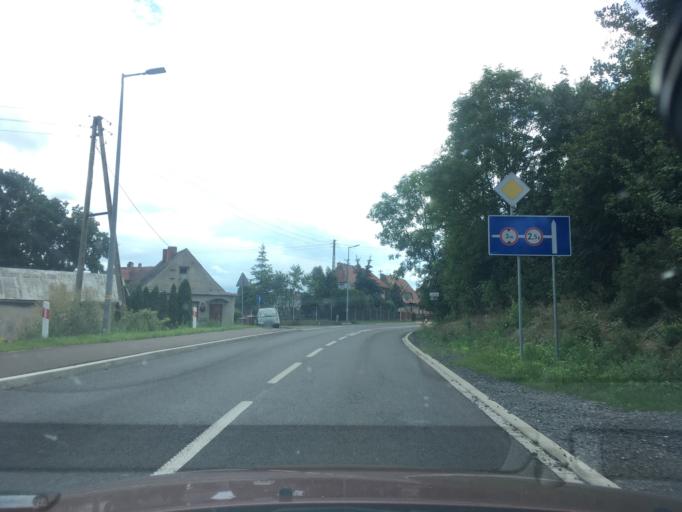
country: PL
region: Lower Silesian Voivodeship
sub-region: Powiat zgorzelecki
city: Zgorzelec
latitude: 51.1841
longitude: 15.0158
